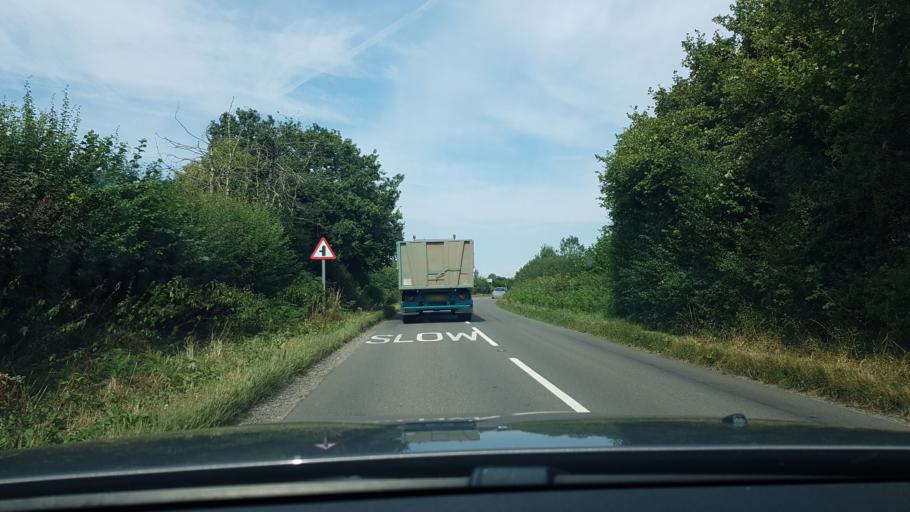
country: GB
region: England
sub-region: West Berkshire
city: Lambourn
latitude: 51.4870
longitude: -1.5478
